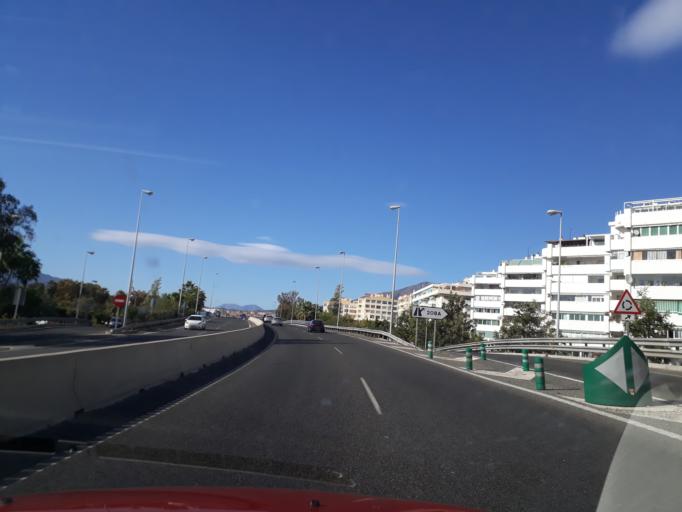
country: ES
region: Andalusia
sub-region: Provincia de Malaga
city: Fuengirola
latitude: 36.5303
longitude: -4.6291
